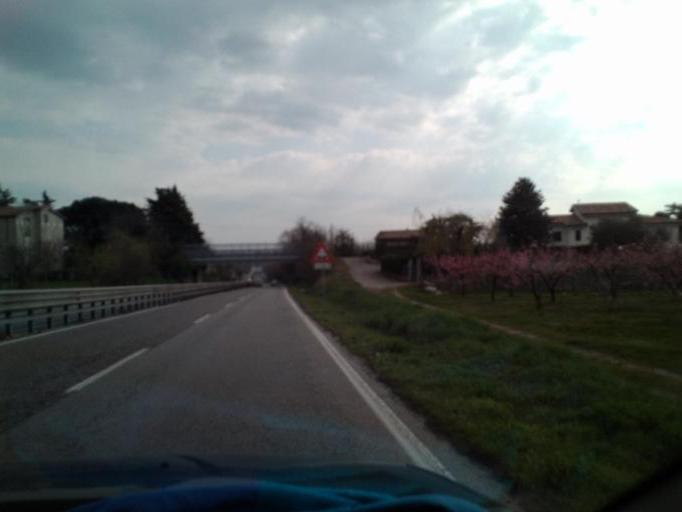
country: IT
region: Veneto
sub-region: Provincia di Verona
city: Pescantina
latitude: 45.4902
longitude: 10.8584
